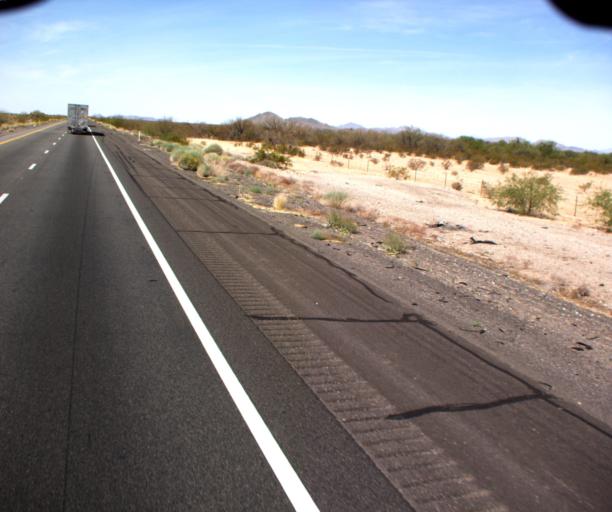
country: US
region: Arizona
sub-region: La Paz County
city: Salome
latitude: 33.5771
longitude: -113.4050
